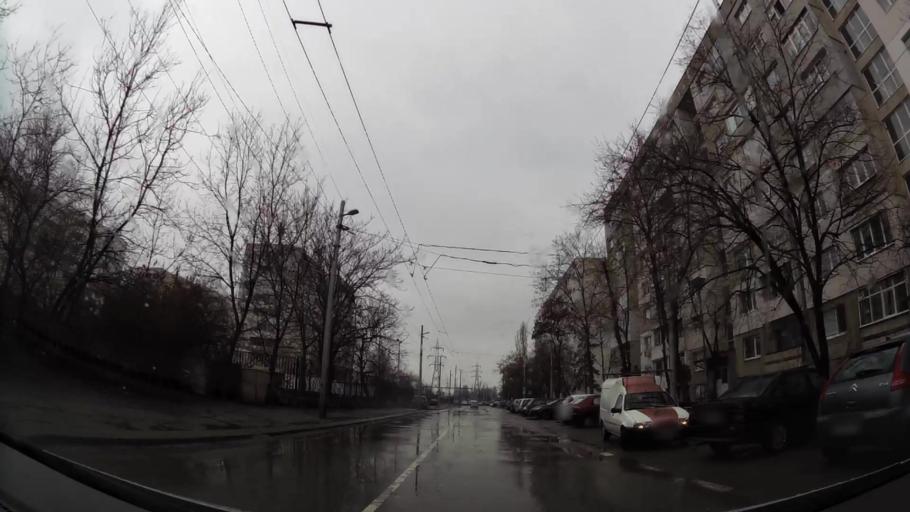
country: BG
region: Sofia-Capital
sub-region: Stolichna Obshtina
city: Sofia
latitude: 42.6701
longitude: 23.3862
